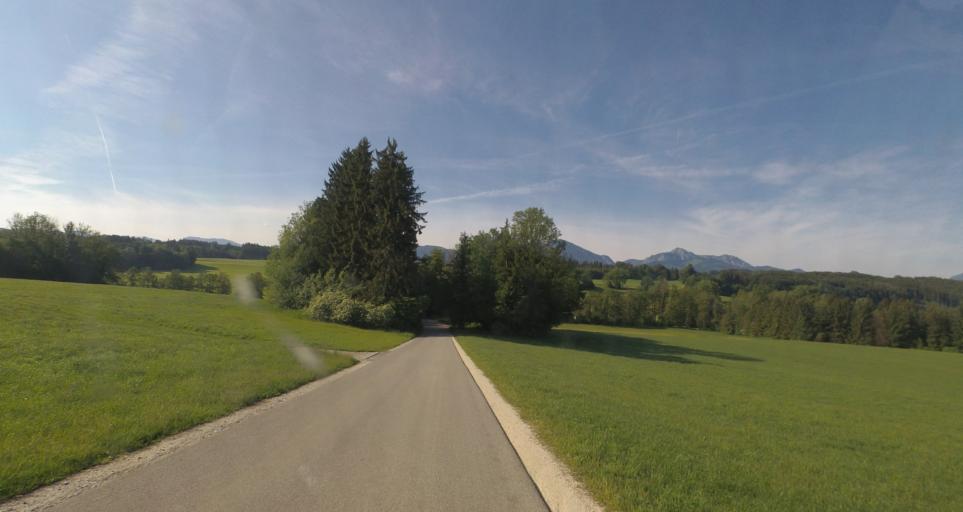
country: DE
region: Bavaria
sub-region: Upper Bavaria
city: Vachendorf
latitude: 47.8487
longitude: 12.5836
